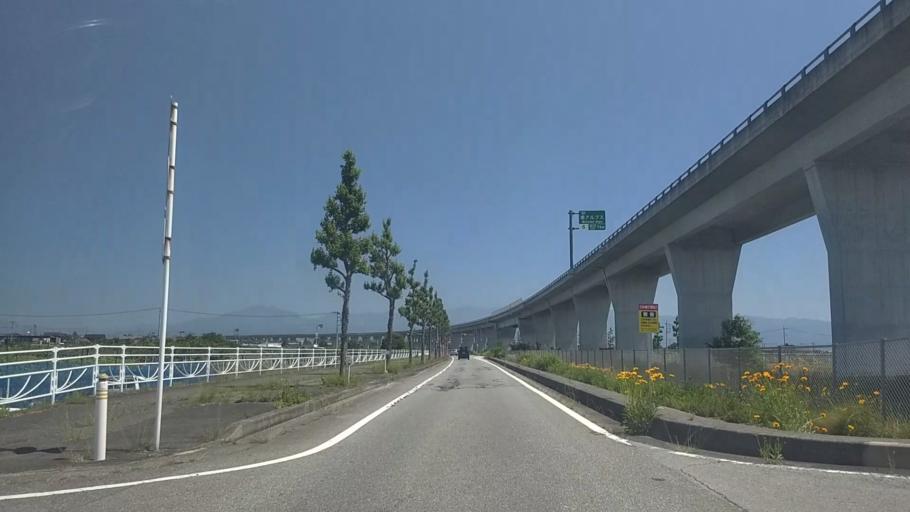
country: JP
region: Yamanashi
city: Ryuo
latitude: 35.6032
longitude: 138.4799
